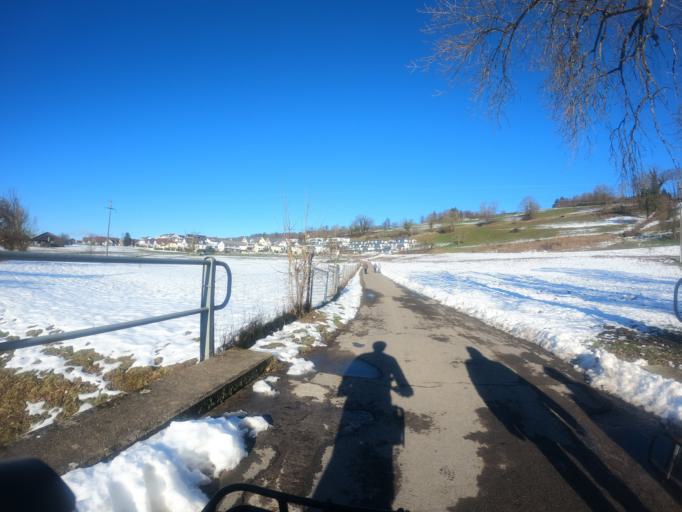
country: CH
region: Aargau
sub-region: Bezirk Bremgarten
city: Unterlunkhofen
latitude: 47.3165
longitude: 8.3831
